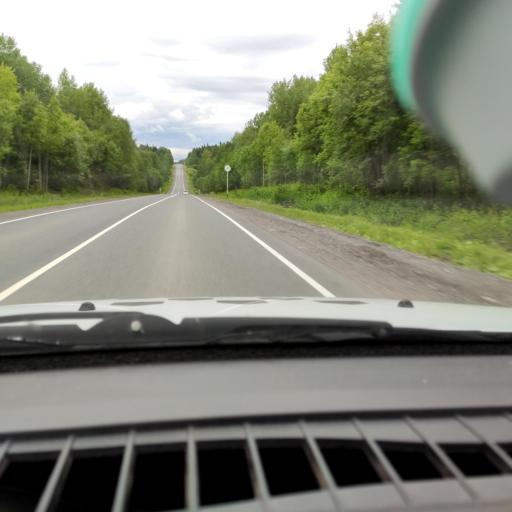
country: RU
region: Perm
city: Chusovoy
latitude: 58.2239
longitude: 57.8252
